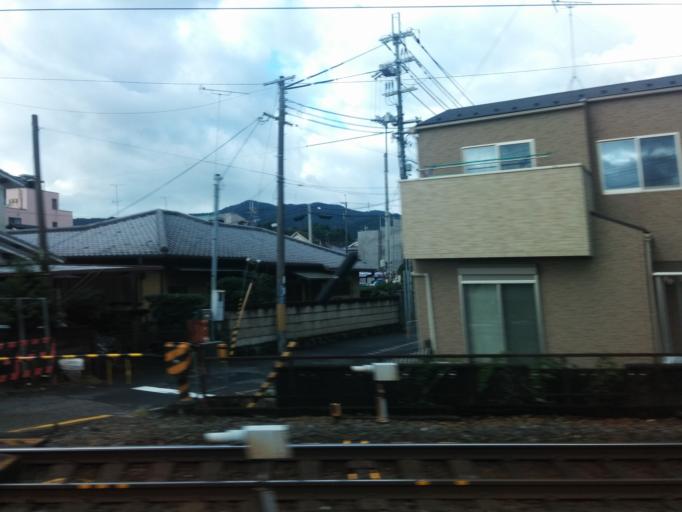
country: JP
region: Shiga Prefecture
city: Otsu-shi
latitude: 34.9832
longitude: 135.8933
